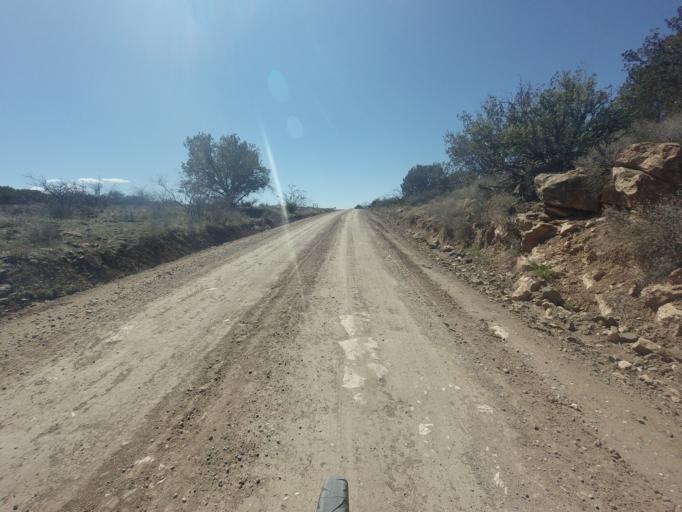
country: US
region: Arizona
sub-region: Yavapai County
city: Lake Montezuma
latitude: 34.6284
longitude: -111.7216
